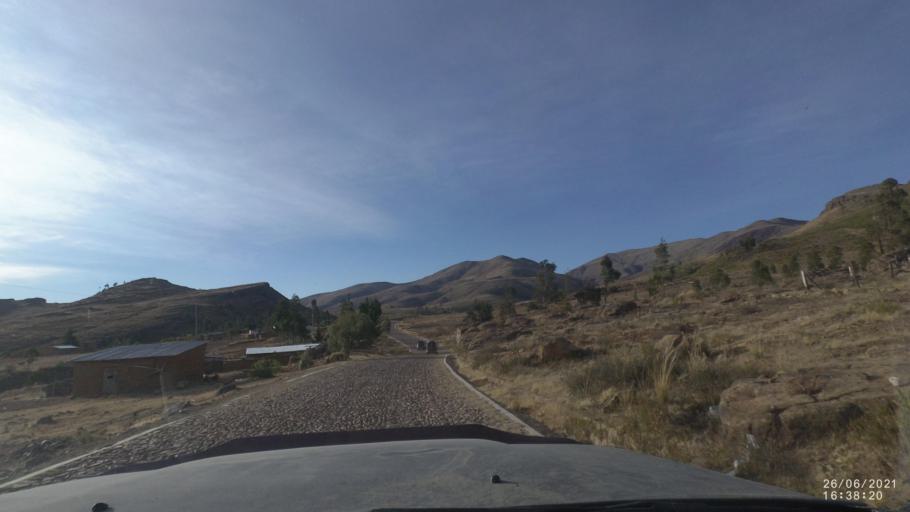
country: BO
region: Cochabamba
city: Arani
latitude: -17.7779
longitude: -65.8140
